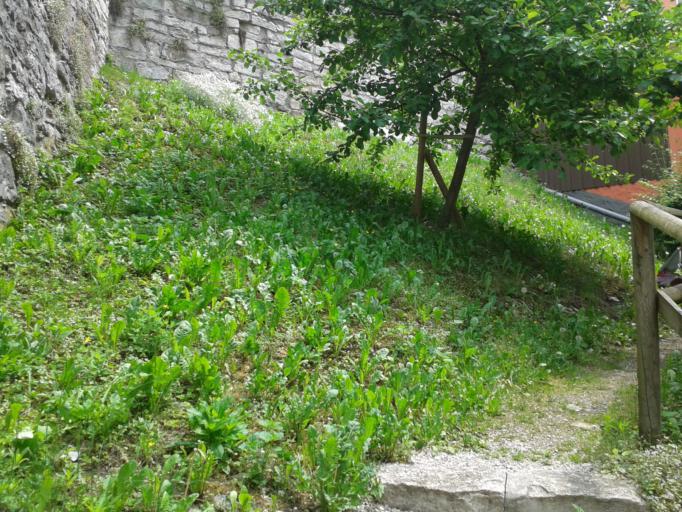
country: DE
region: Bavaria
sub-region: Upper Franconia
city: Grafenberg
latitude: 49.6443
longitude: 11.2485
